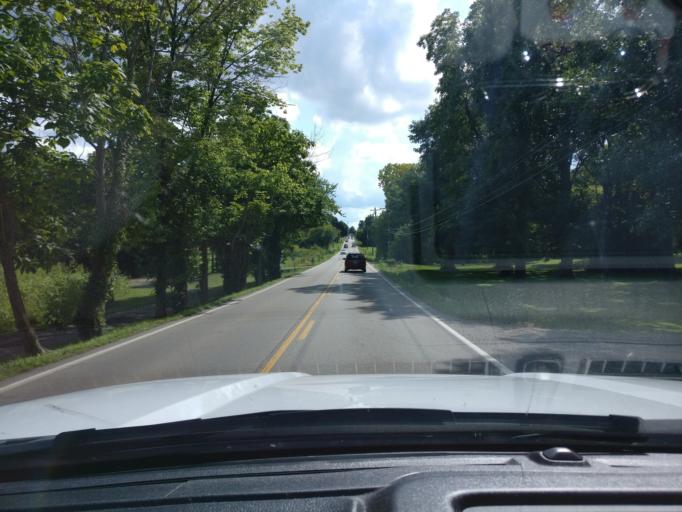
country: US
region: Ohio
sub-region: Warren County
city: Five Points
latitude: 39.5139
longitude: -84.1890
